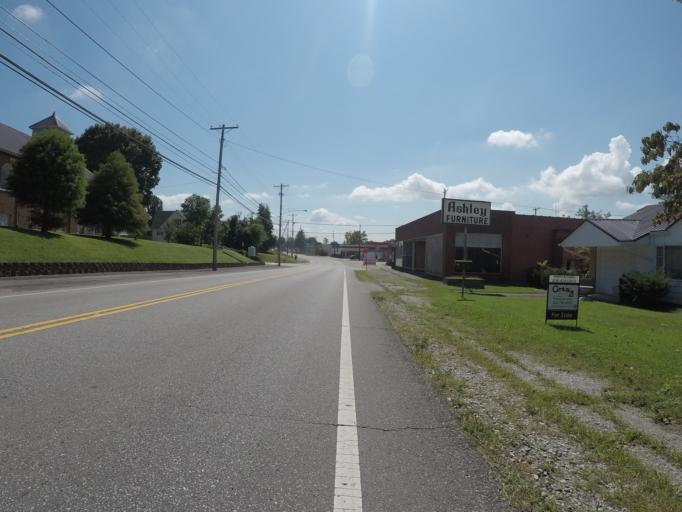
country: US
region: Ohio
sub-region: Lawrence County
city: South Point
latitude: 38.4199
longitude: -82.5884
